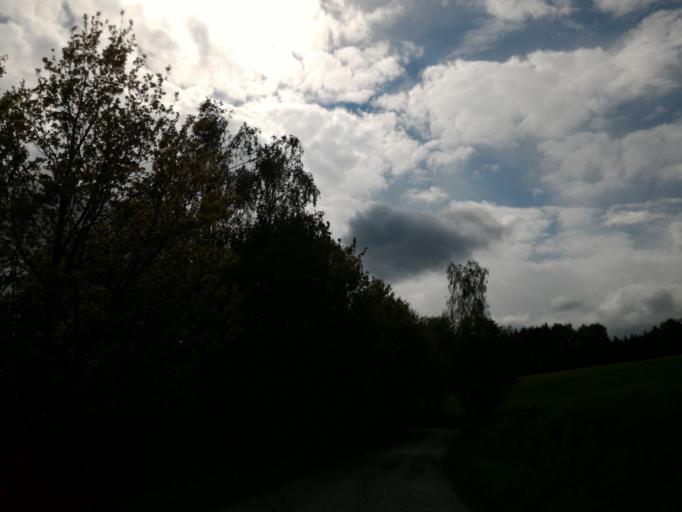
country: CZ
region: Vysocina
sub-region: Okres Havlickuv Brod
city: Svetla nad Sazavou
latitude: 49.6234
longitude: 15.3346
